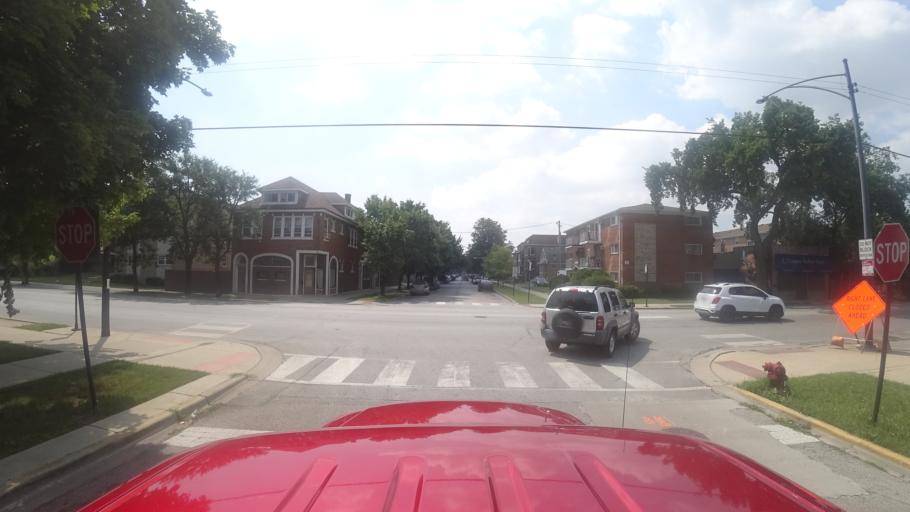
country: US
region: Illinois
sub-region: Cook County
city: Cicero
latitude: 41.8081
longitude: -87.7212
